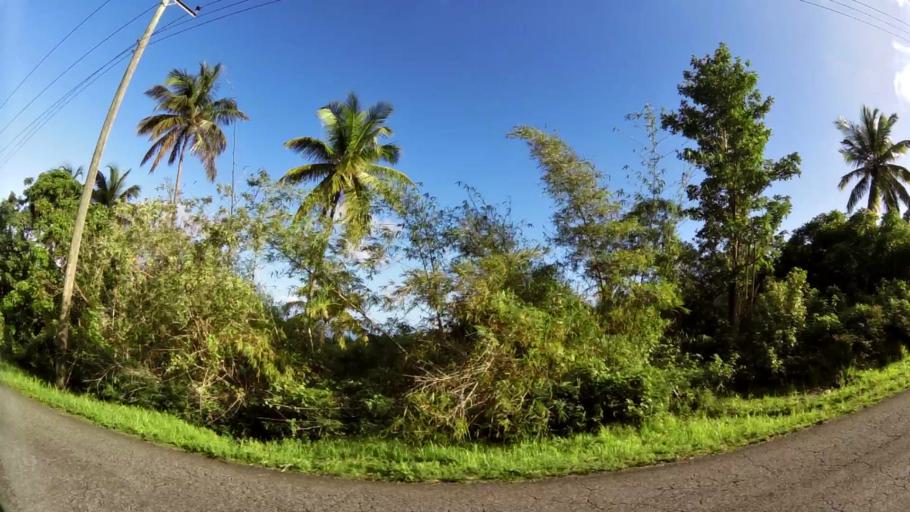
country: LC
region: Anse-la-Raye
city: Canaries
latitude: 13.9159
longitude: -61.0493
